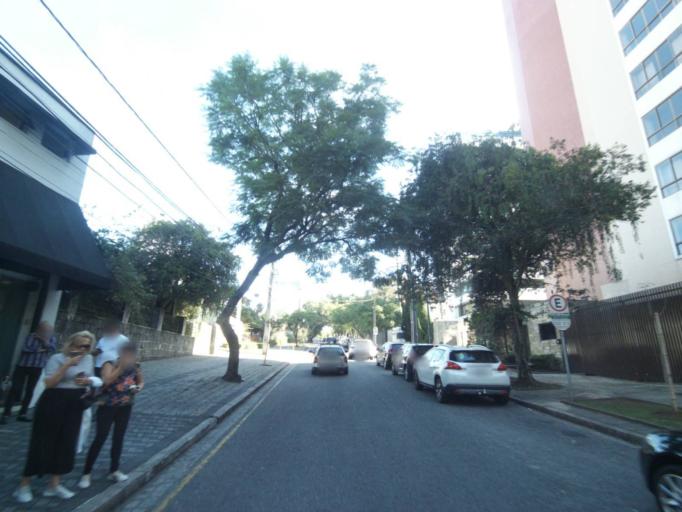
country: BR
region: Parana
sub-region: Curitiba
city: Curitiba
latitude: -25.4384
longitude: -49.2868
